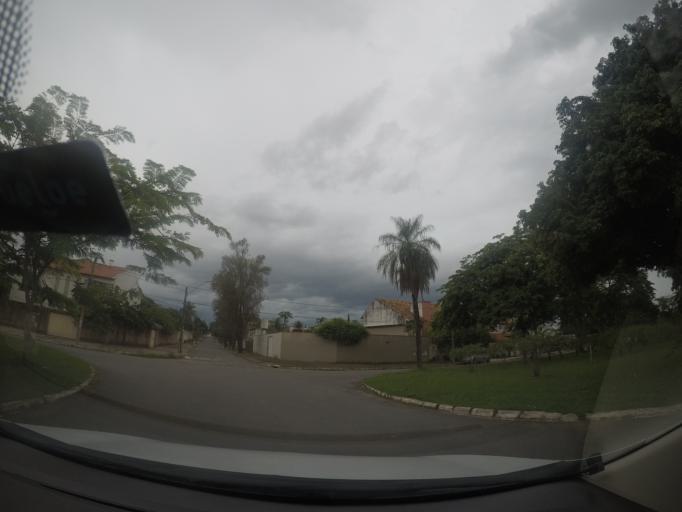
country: BR
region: Goias
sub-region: Goiania
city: Goiania
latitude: -16.6508
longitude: -49.2334
